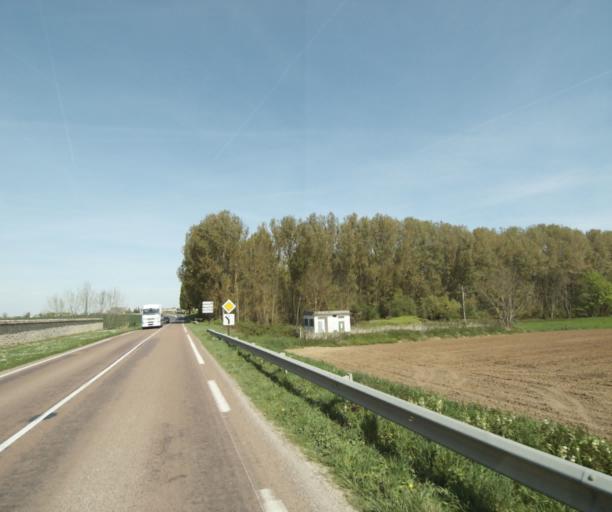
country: FR
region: Ile-de-France
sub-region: Departement de Seine-et-Marne
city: Nangis
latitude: 48.5431
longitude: 3.0174
